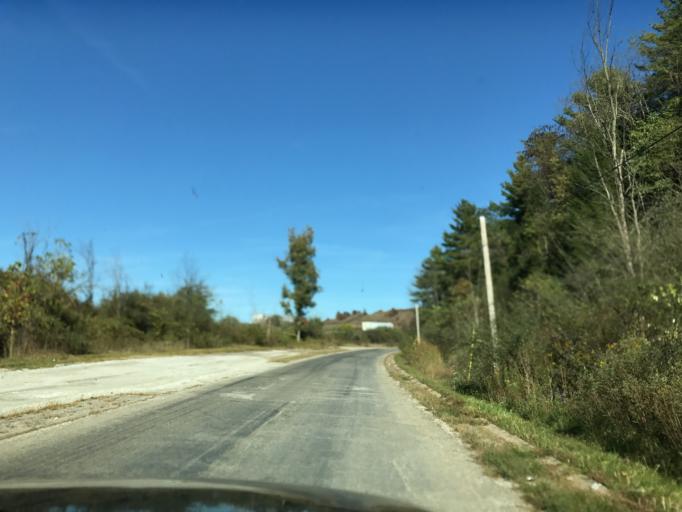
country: US
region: Ohio
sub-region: Belmont County
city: Barnesville
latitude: 40.0576
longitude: -81.1464
